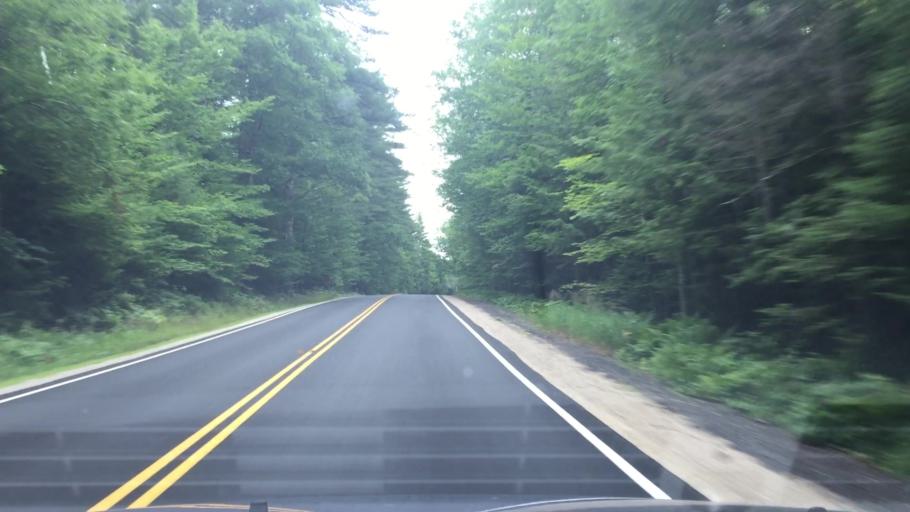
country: US
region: New Hampshire
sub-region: Carroll County
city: Freedom
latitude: 43.8417
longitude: -71.0820
